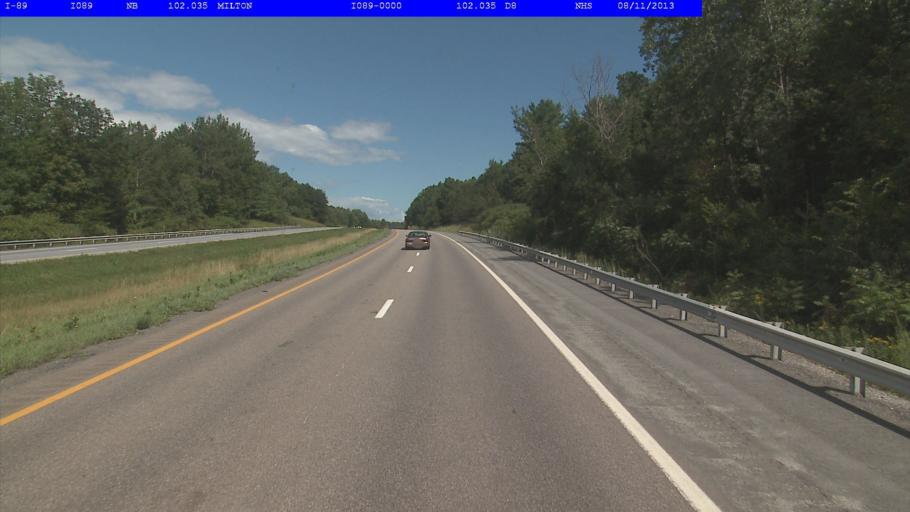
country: US
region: Vermont
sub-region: Chittenden County
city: Milton
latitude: 44.6428
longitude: -73.1393
